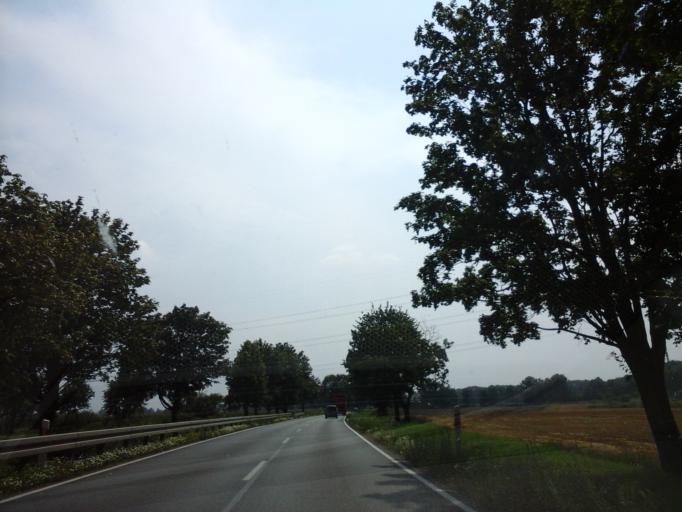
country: PL
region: Lower Silesian Voivodeship
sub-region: Powiat wroclawski
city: Zorawina
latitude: 50.9515
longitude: 17.0710
